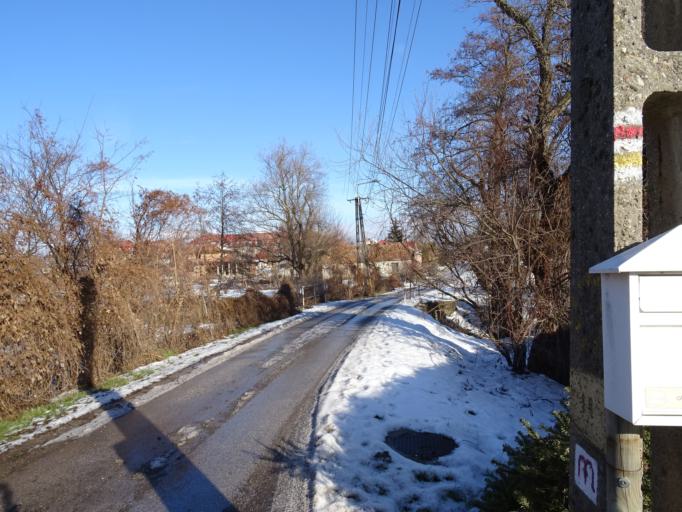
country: HU
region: Komarom-Esztergom
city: Oroszlany
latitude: 47.4897
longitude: 18.3230
